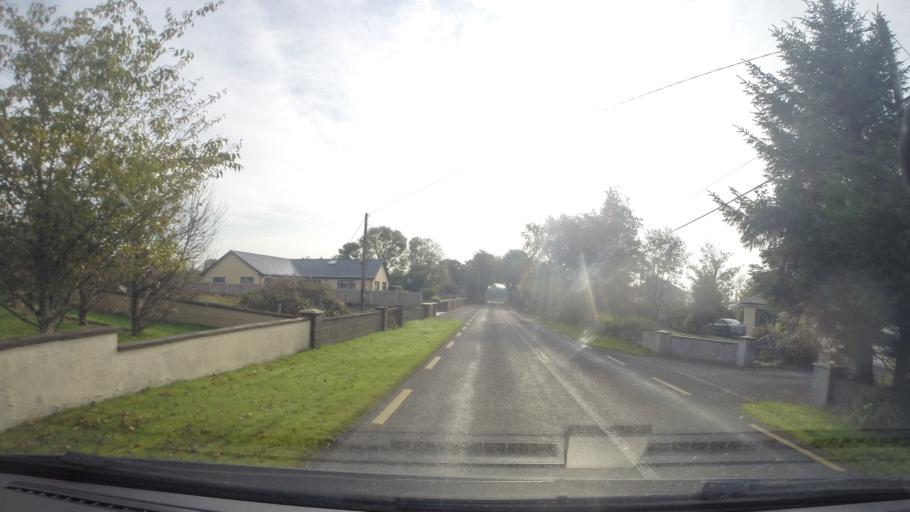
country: IE
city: Ballisodare
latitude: 54.2394
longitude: -8.5381
